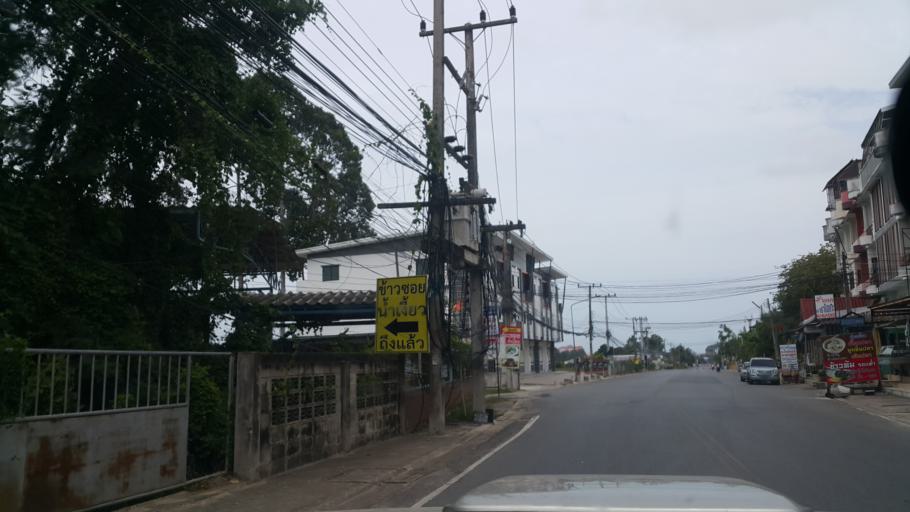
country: TH
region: Rayong
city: Ban Chang
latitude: 12.7176
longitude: 101.0493
